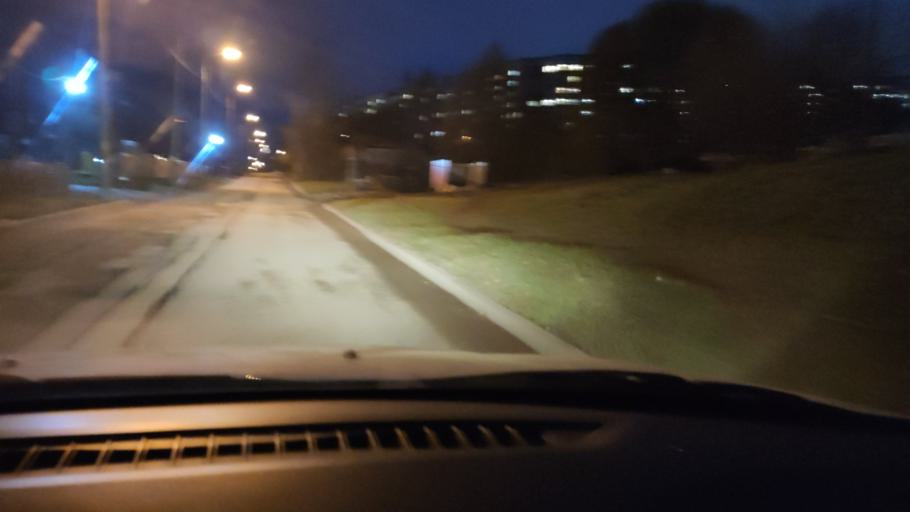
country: RU
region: Perm
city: Perm
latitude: 58.0098
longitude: 56.3135
